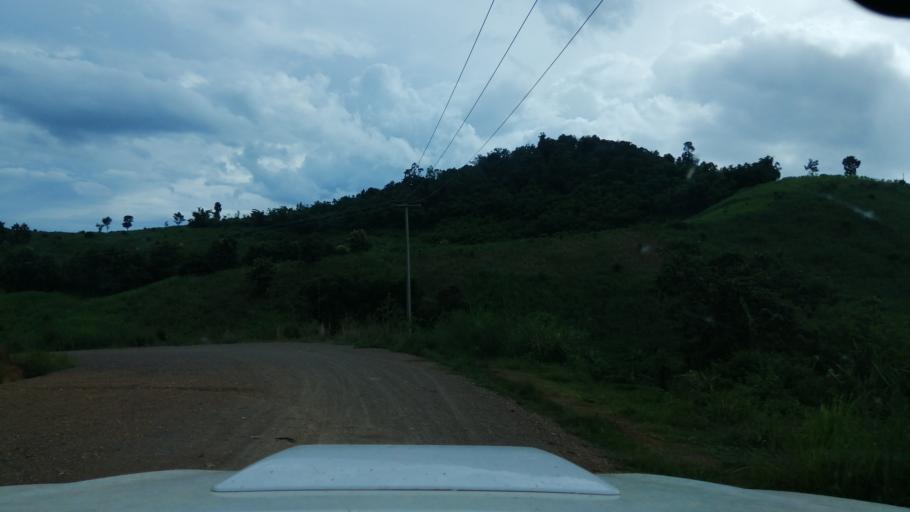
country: TH
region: Nan
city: Song Khwae
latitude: 19.5459
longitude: 100.6995
